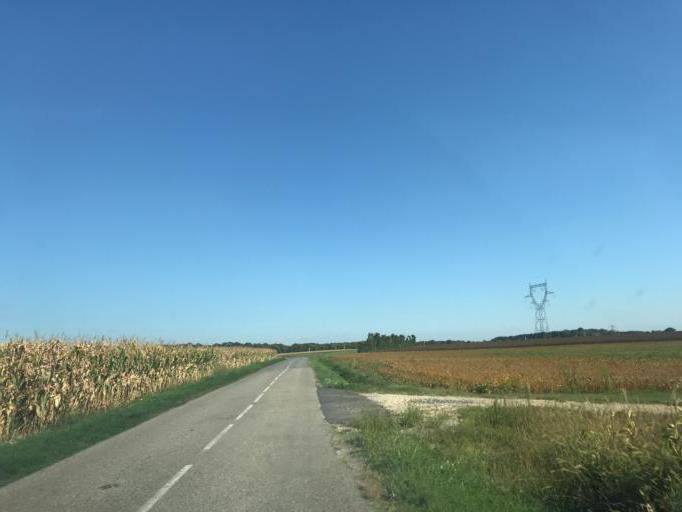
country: FR
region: Rhone-Alpes
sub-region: Departement de l'Ain
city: Beynost
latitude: 45.8640
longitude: 4.9942
